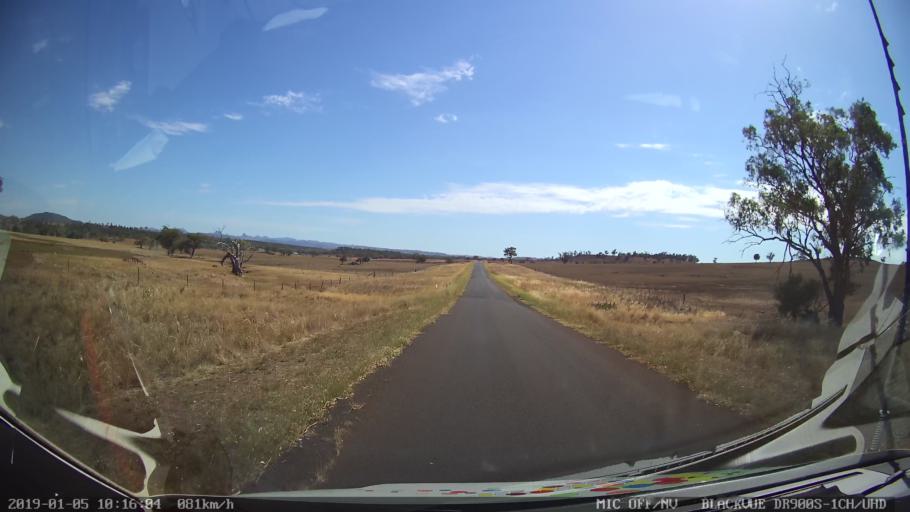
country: AU
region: New South Wales
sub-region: Gilgandra
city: Gilgandra
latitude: -31.5788
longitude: 148.9490
